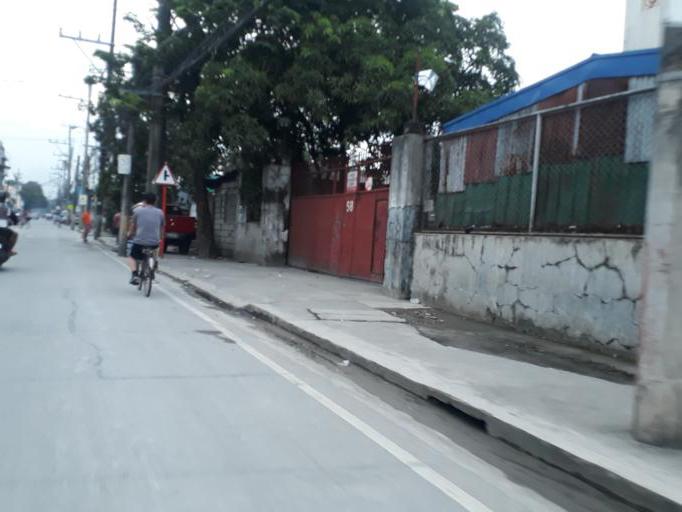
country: PH
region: Calabarzon
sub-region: Province of Rizal
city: Valenzuela
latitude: 14.7007
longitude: 120.9508
